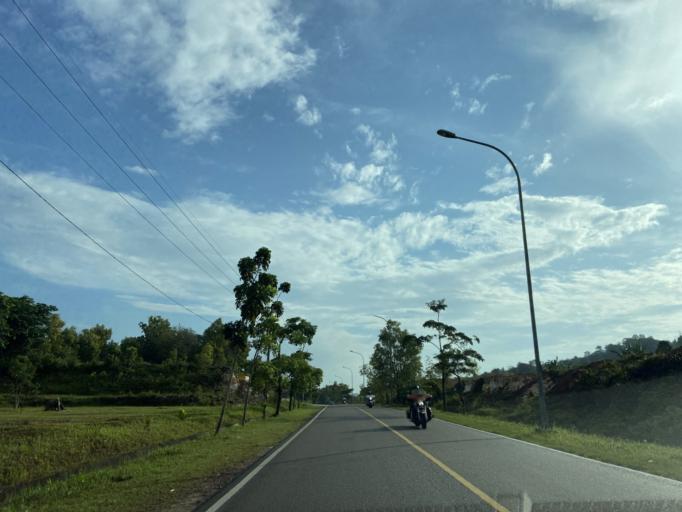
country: SG
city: Singapore
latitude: 0.9595
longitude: 104.0544
